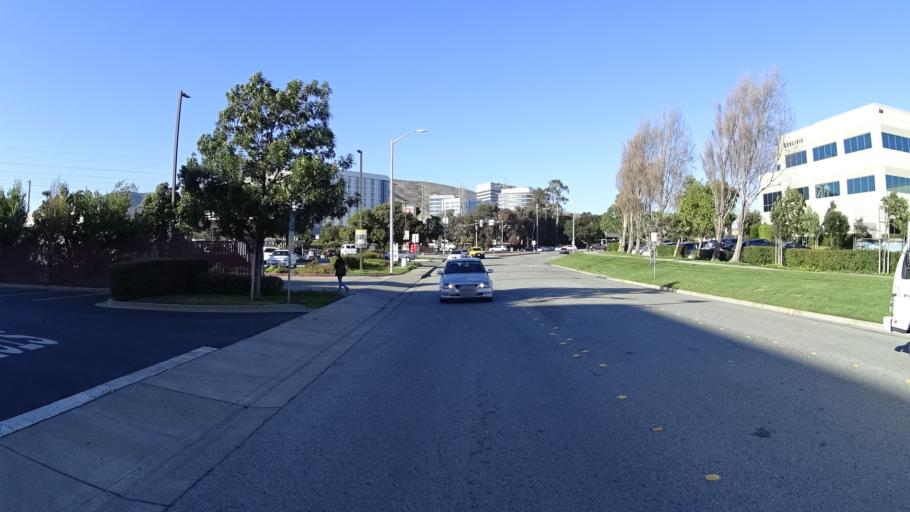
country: US
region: California
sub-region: San Mateo County
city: South San Francisco
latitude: 37.6533
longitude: -122.4002
